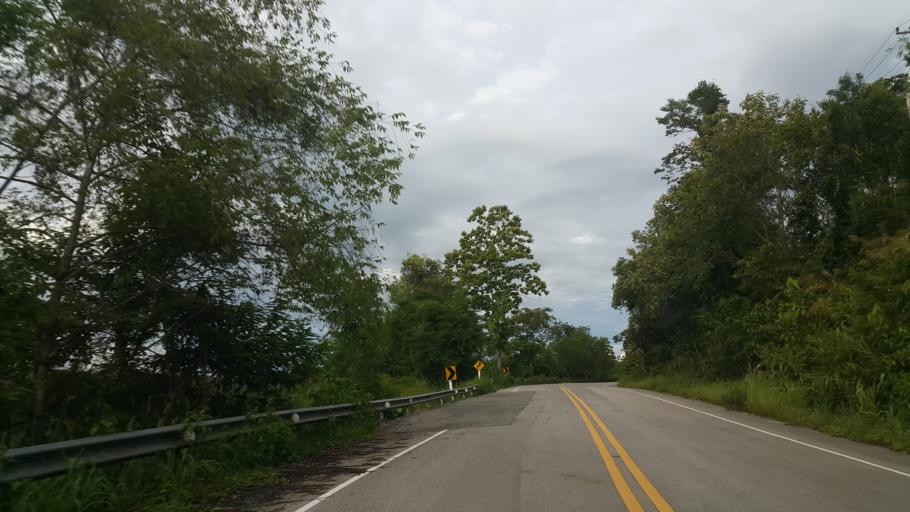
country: TH
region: Loei
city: Na Haeo
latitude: 17.5037
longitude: 101.0886
